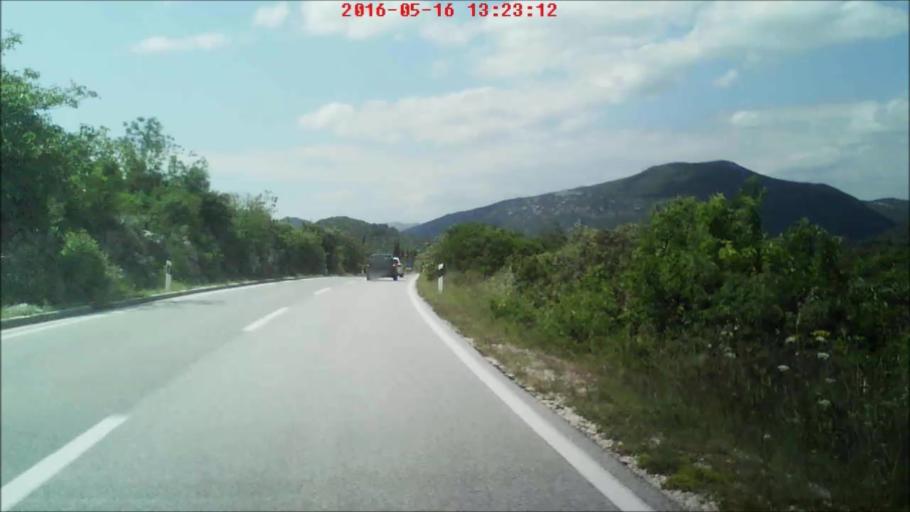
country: HR
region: Dubrovacko-Neretvanska
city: Ston
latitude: 42.8403
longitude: 17.7153
